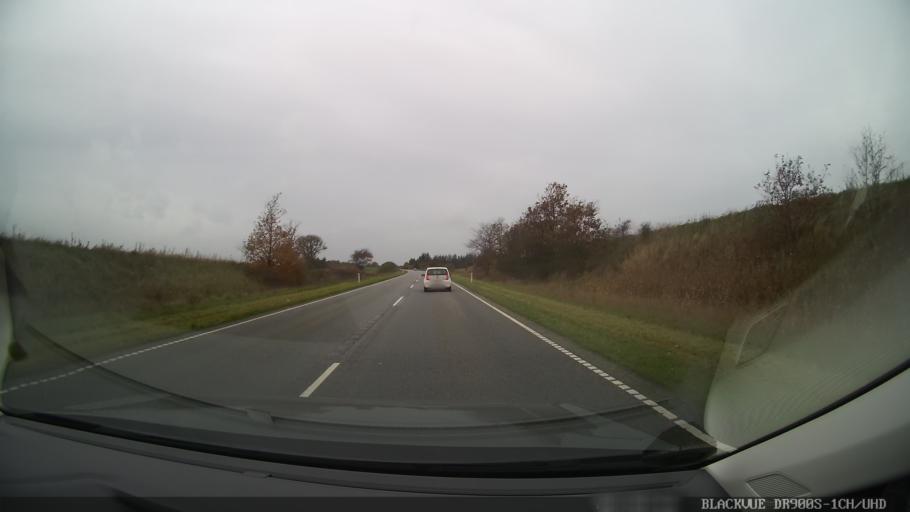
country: DK
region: North Denmark
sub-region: Morso Kommune
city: Nykobing Mors
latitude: 56.8236
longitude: 8.7599
